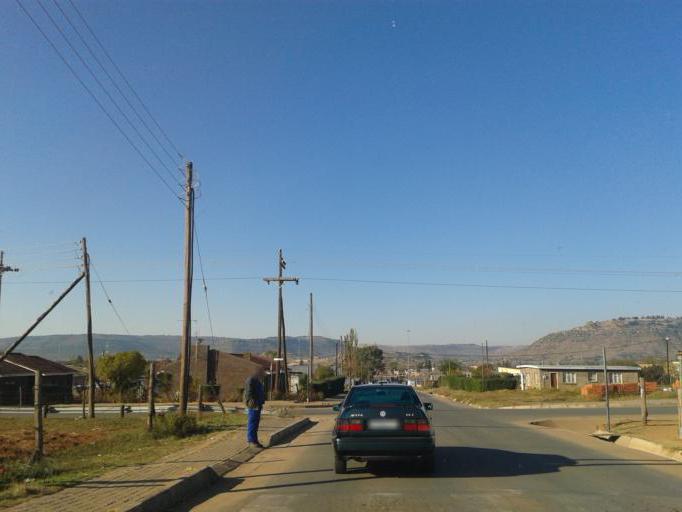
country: LS
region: Maseru
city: Maseru
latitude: -29.2766
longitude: 27.5328
